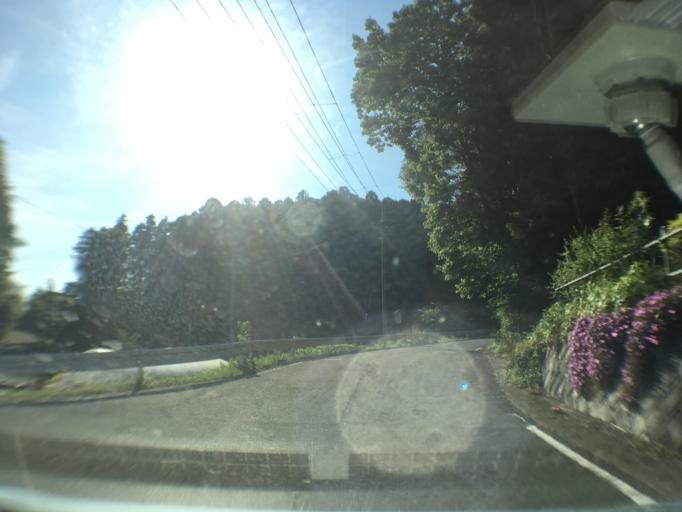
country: JP
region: Miyagi
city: Wakuya
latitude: 38.6203
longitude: 141.2917
